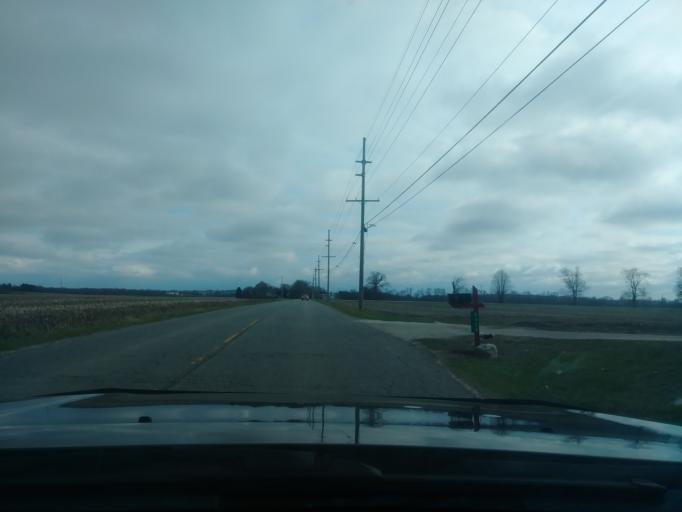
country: US
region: Indiana
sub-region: LaPorte County
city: LaPorte
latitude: 41.6127
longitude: -86.7972
